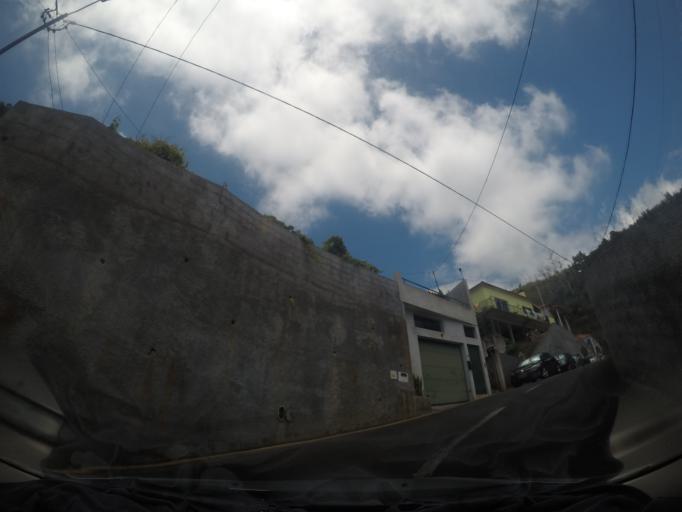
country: PT
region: Madeira
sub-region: Funchal
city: Nossa Senhora do Monte
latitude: 32.6763
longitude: -16.9237
